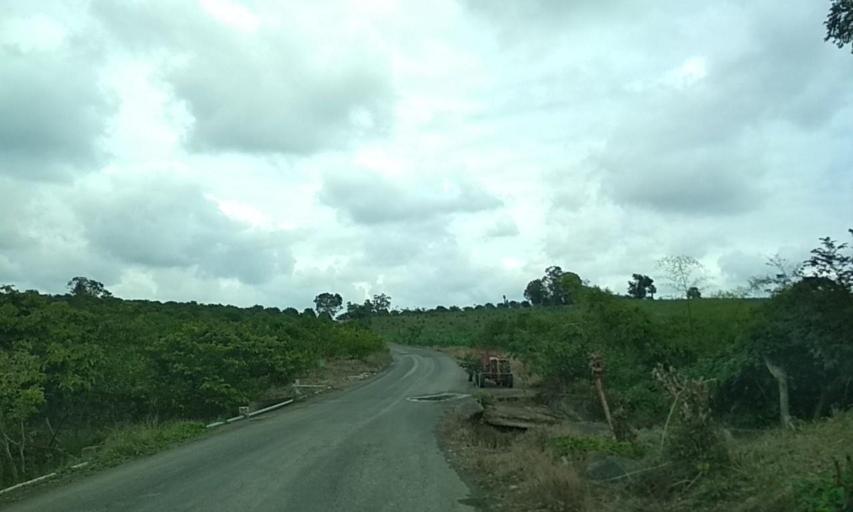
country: MX
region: Veracruz
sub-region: Papantla
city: El Chote
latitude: 20.3364
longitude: -97.3981
